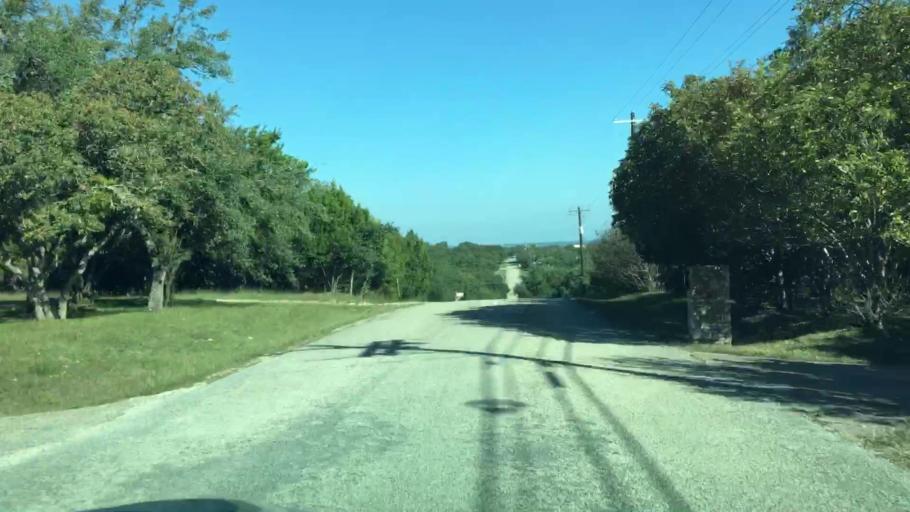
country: US
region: Texas
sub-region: Hays County
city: Dripping Springs
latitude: 30.1908
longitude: -98.0190
